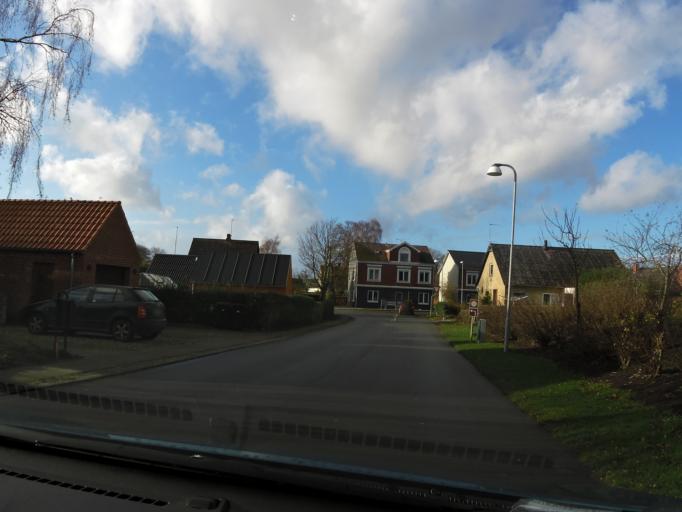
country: DK
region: Central Jutland
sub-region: Odder Kommune
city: Odder
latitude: 55.8921
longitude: 10.1683
